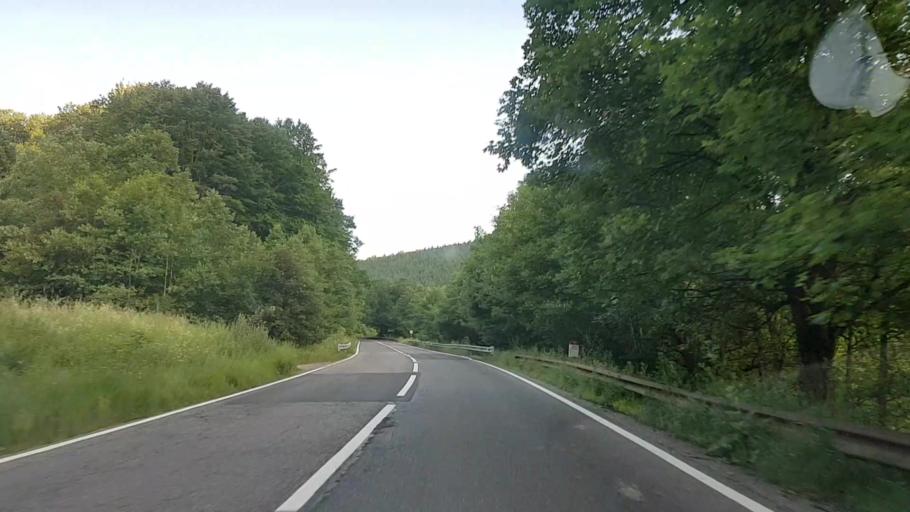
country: RO
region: Harghita
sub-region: Comuna Corund
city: Corund
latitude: 46.4565
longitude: 25.2106
